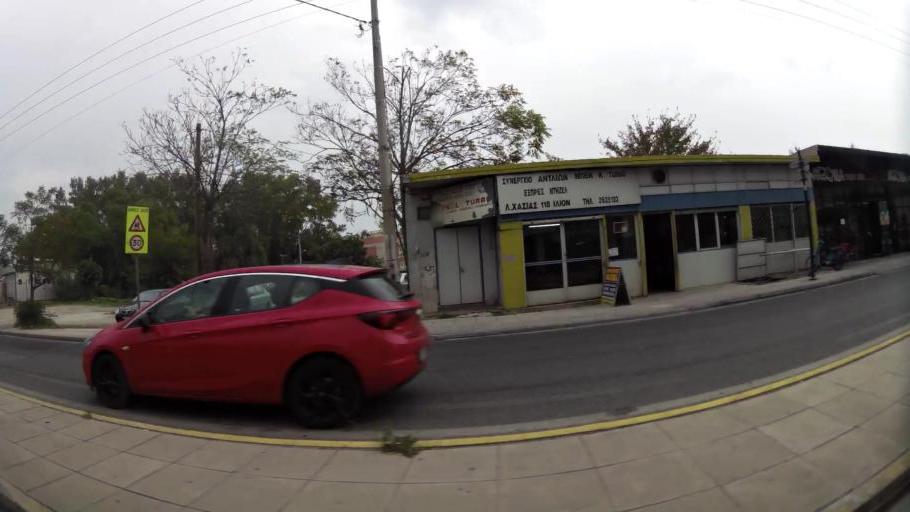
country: GR
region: Attica
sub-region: Nomarchia Athinas
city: Agioi Anargyroi
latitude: 38.0362
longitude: 23.7164
